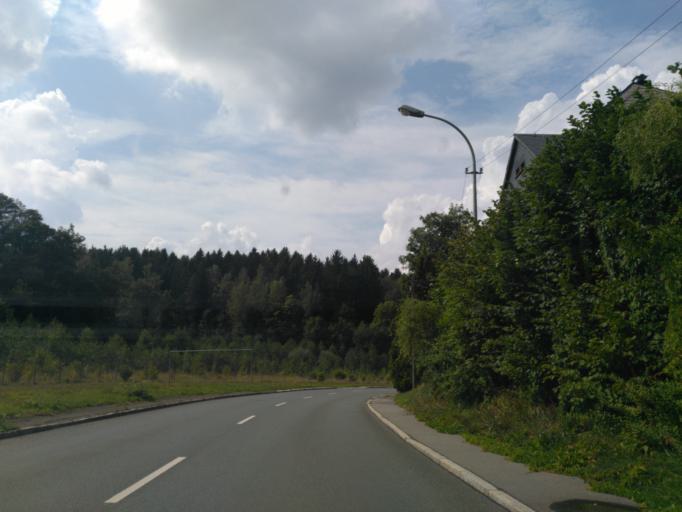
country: DE
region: Saxony
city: Rodewisch
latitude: 50.5308
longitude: 12.4402
